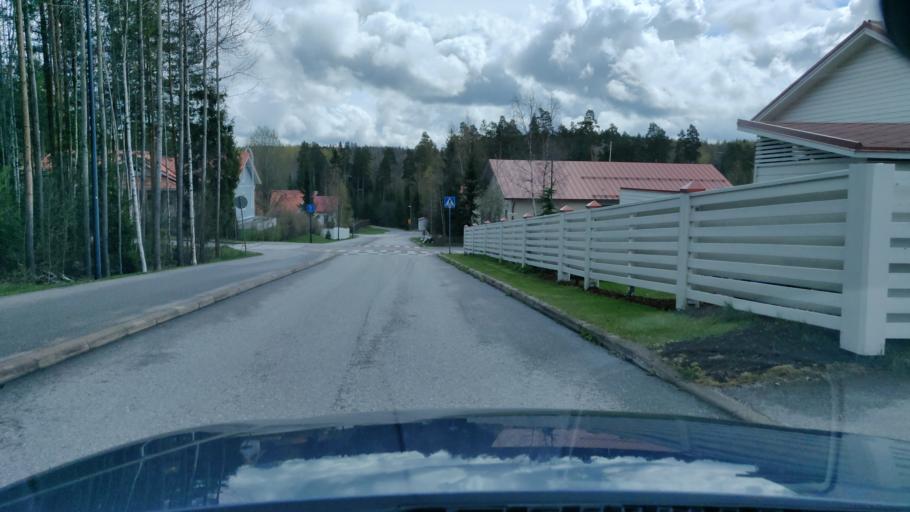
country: FI
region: Uusimaa
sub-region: Helsinki
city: Nurmijaervi
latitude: 60.3625
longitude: 24.7268
